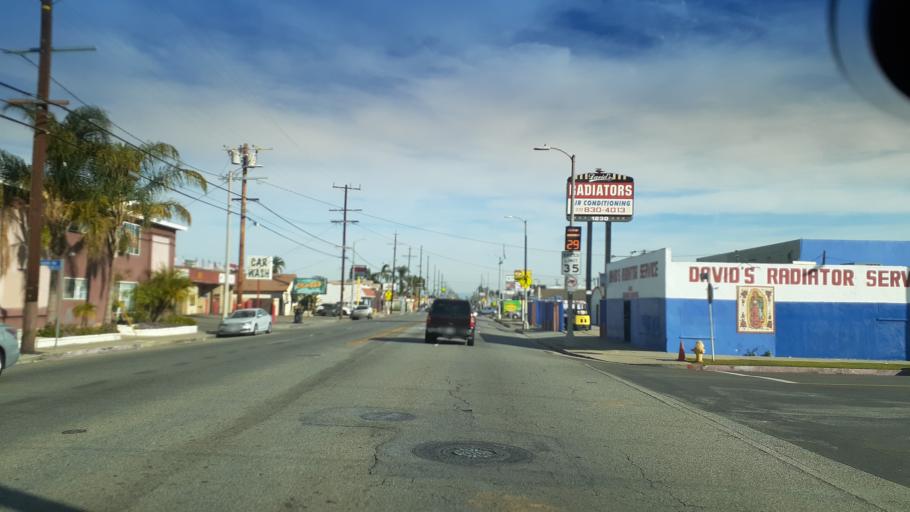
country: US
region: California
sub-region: Los Angeles County
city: Lomita
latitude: 33.7791
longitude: -118.2781
